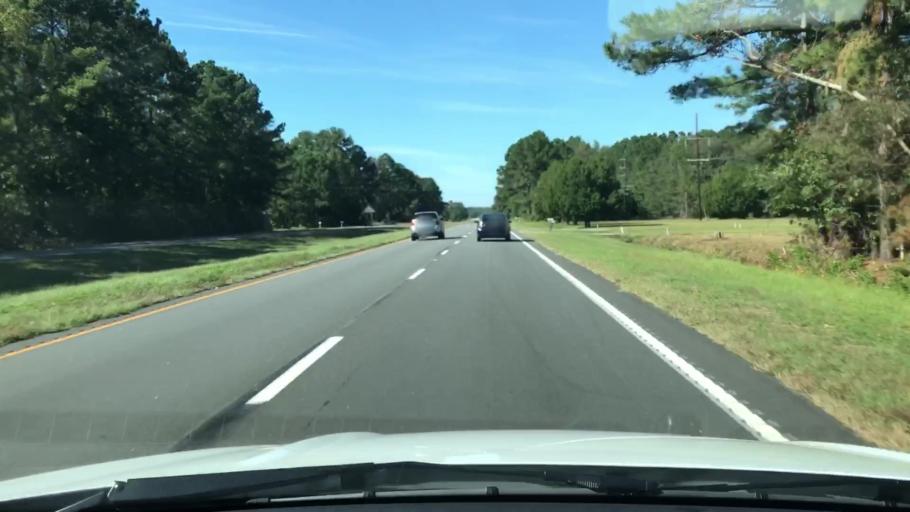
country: US
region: South Carolina
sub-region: Hampton County
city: Yemassee
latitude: 32.5918
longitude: -80.7496
